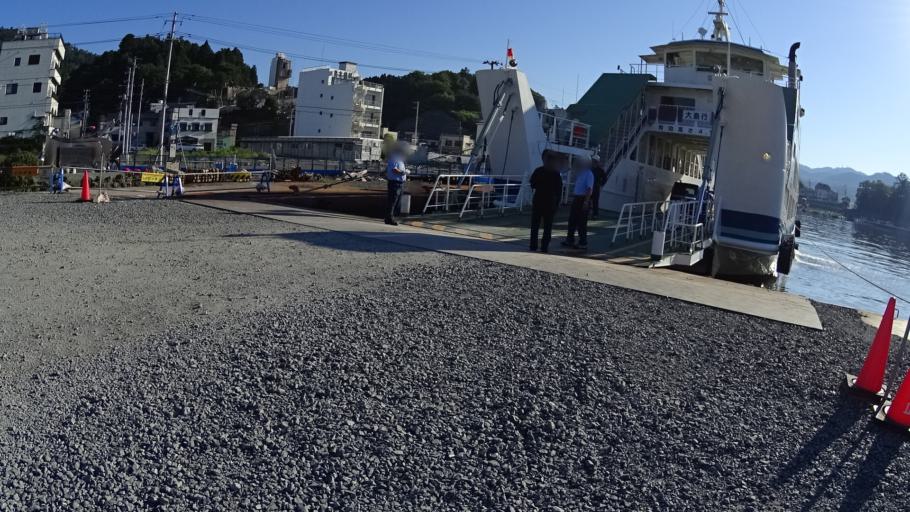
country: JP
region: Iwate
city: Ofunato
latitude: 38.9060
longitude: 141.5750
